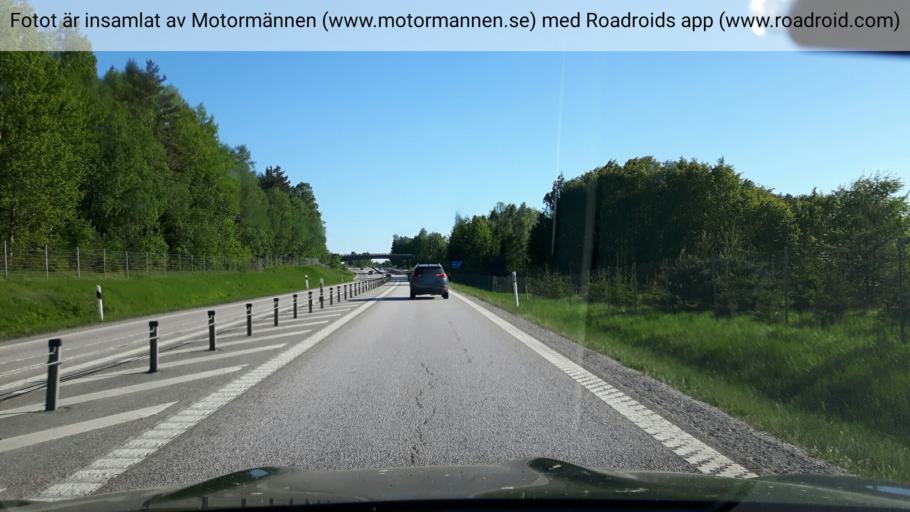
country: SE
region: Stockholm
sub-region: Vallentuna Kommun
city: Vallentuna
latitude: 59.5148
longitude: 18.1775
